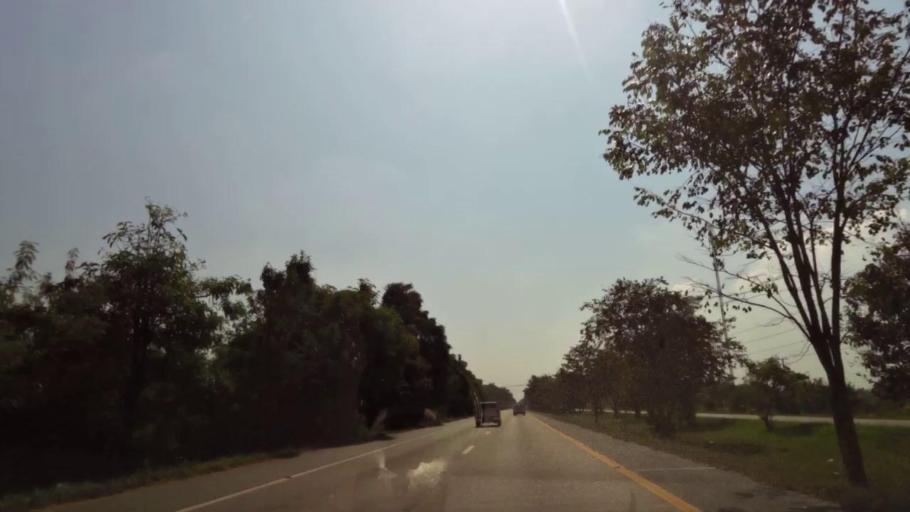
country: TH
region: Phichit
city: Wachira Barami
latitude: 16.5771
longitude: 100.1480
